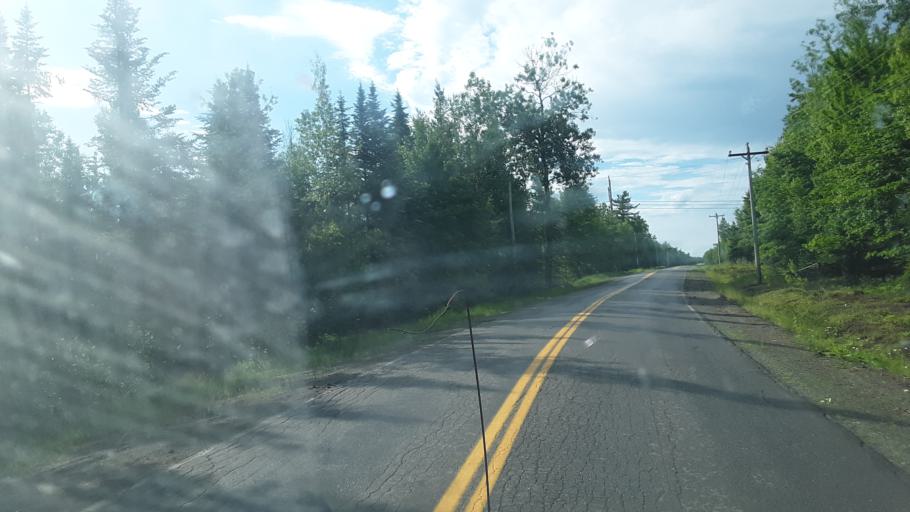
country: US
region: Maine
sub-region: Washington County
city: Calais
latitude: 45.1917
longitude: -67.5222
